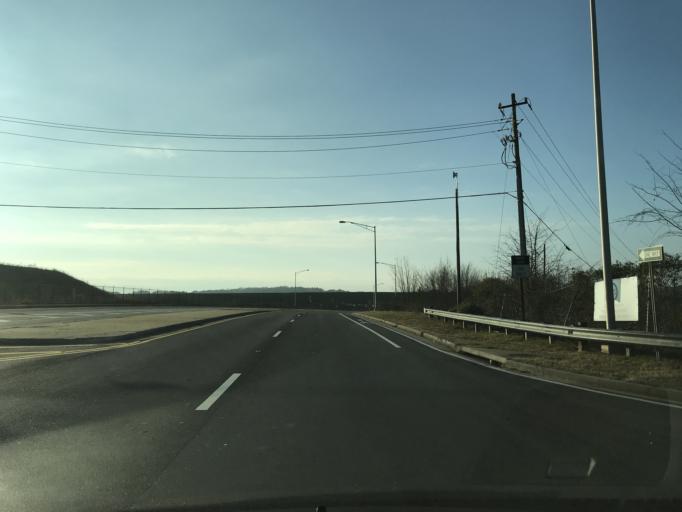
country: US
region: Georgia
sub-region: Fulton County
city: College Park
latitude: 33.6248
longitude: -84.4463
